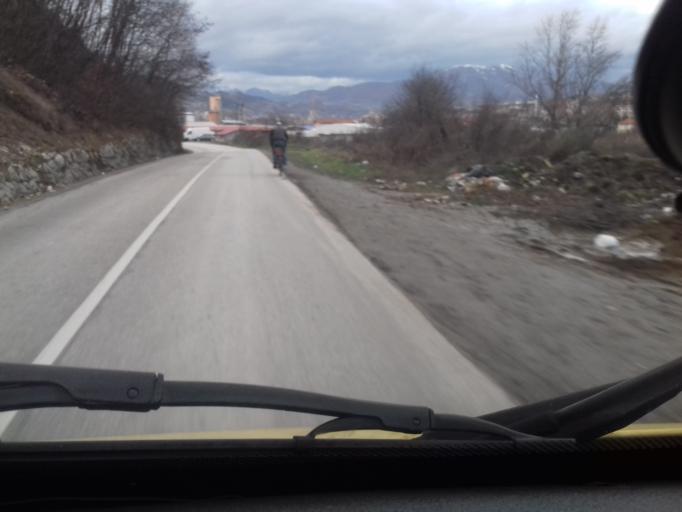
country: BA
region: Federation of Bosnia and Herzegovina
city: Zenica
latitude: 44.1881
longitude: 17.9382
